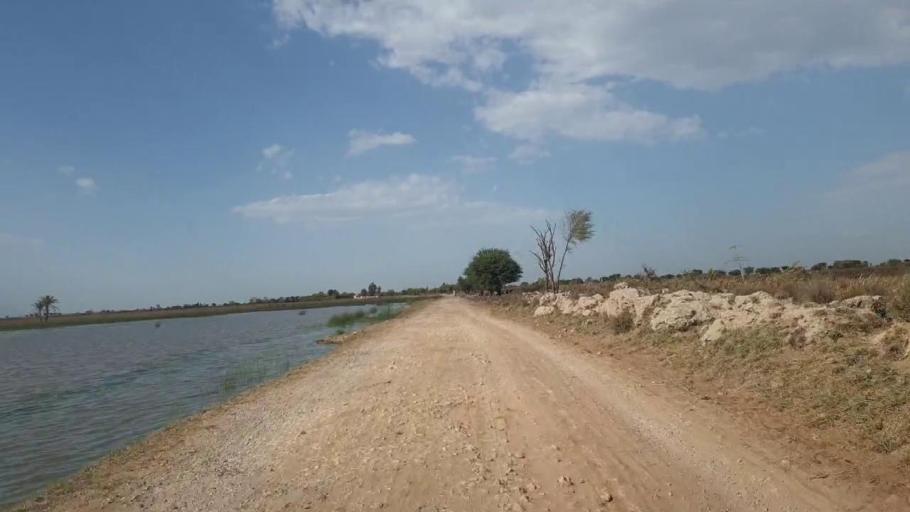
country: PK
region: Sindh
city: Shahdadpur
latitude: 25.9992
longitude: 68.4615
